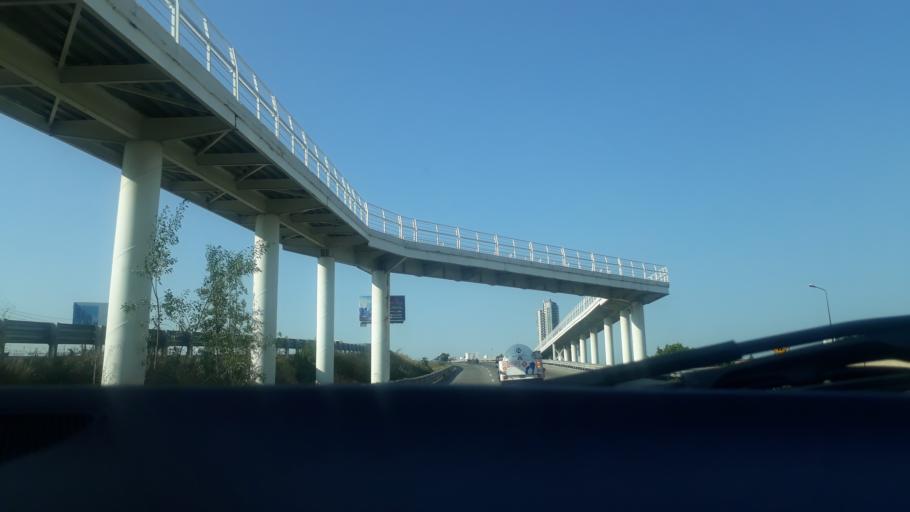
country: MX
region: Puebla
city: Tlazcalancingo
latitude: 19.0053
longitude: -98.2603
